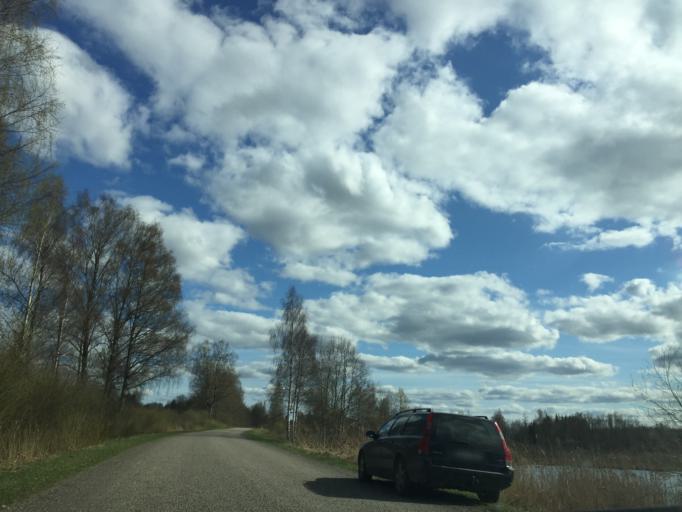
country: LV
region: Rezekne
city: Rezekne
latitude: 56.6209
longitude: 27.3151
